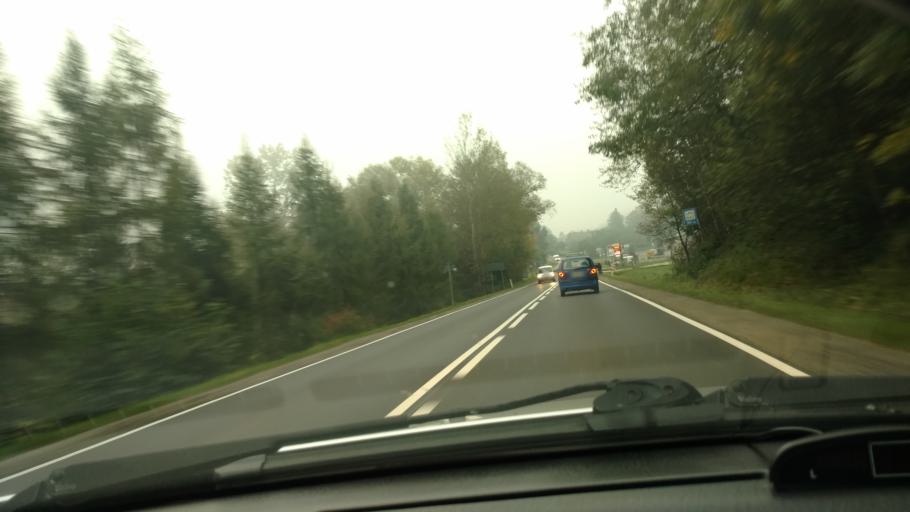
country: PL
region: Subcarpathian Voivodeship
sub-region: Powiat strzyzowski
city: Frysztak
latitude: 49.8346
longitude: 21.6131
